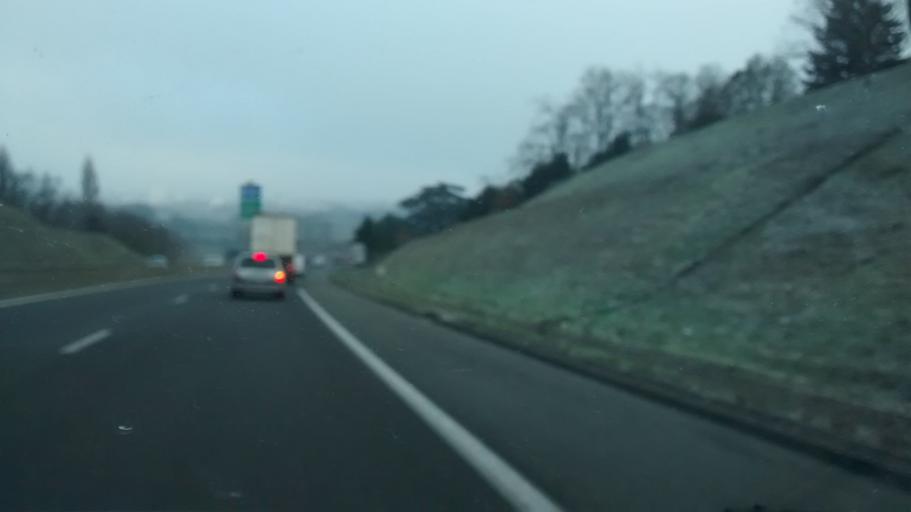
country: FR
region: Centre
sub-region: Departement d'Indre-et-Loire
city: Joue-les-Tours
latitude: 47.3647
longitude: 0.6506
